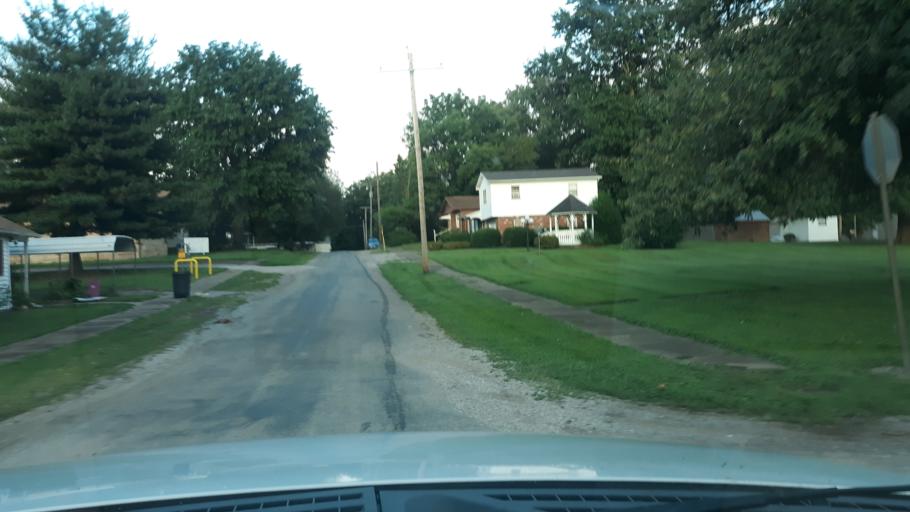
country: US
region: Illinois
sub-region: Saline County
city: Eldorado
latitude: 37.8152
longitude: -88.4355
